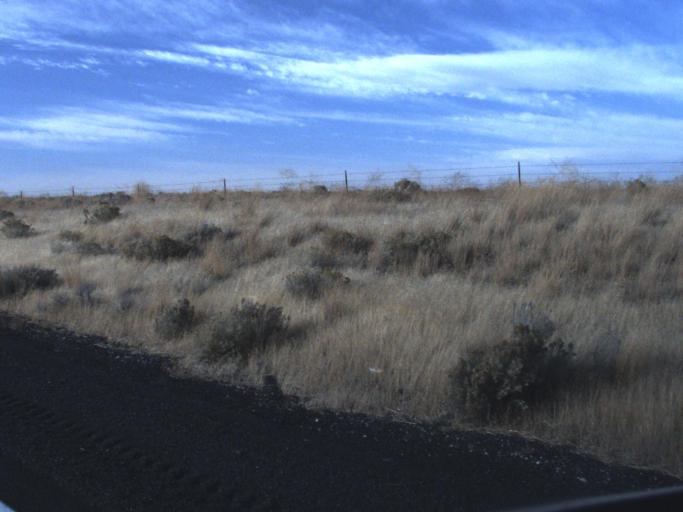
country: US
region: Washington
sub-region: Grant County
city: Warden
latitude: 47.3483
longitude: -118.9297
